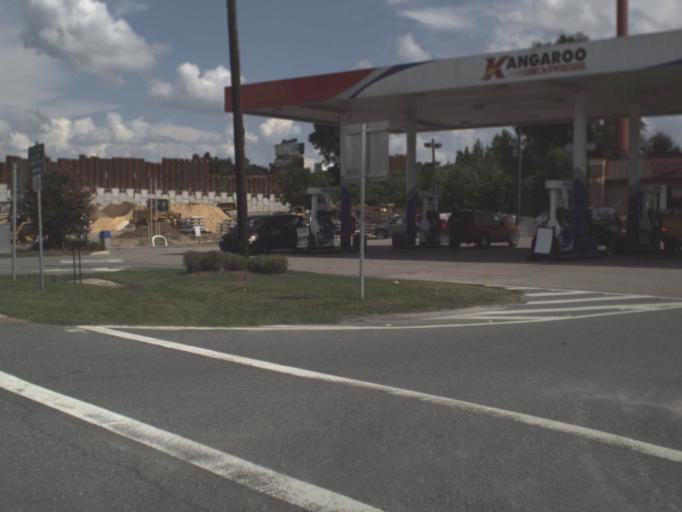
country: US
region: Florida
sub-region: Alachua County
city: High Springs
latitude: 29.8020
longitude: -82.5159
